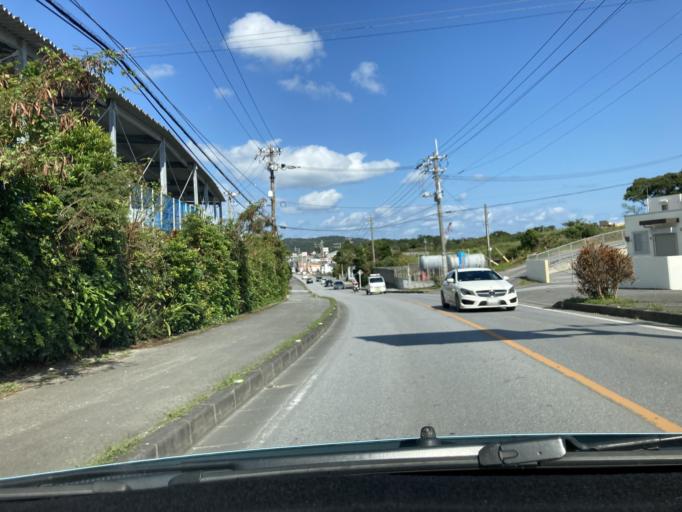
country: JP
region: Okinawa
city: Nago
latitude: 26.6138
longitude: 128.0006
